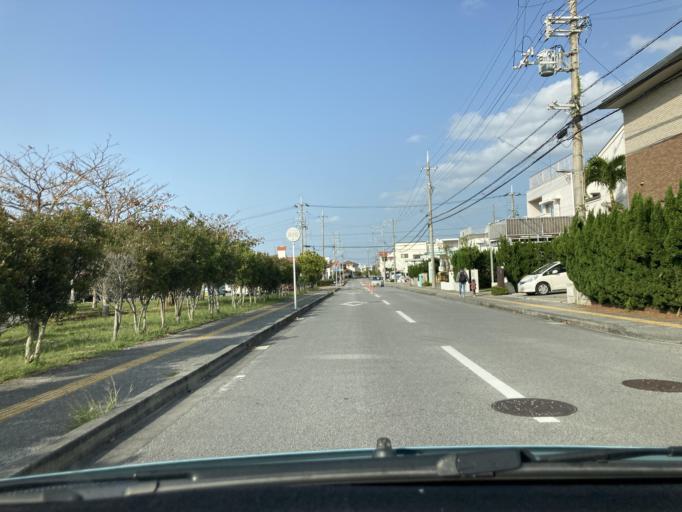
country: JP
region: Okinawa
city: Ginowan
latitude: 26.2074
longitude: 127.7603
